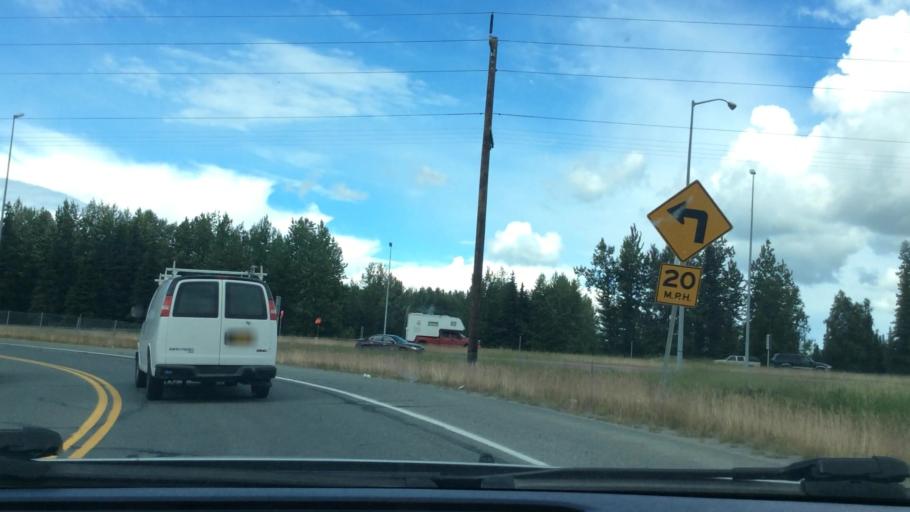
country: US
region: Alaska
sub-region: Anchorage Municipality
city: Elmendorf Air Force Base
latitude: 61.2237
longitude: -149.7567
